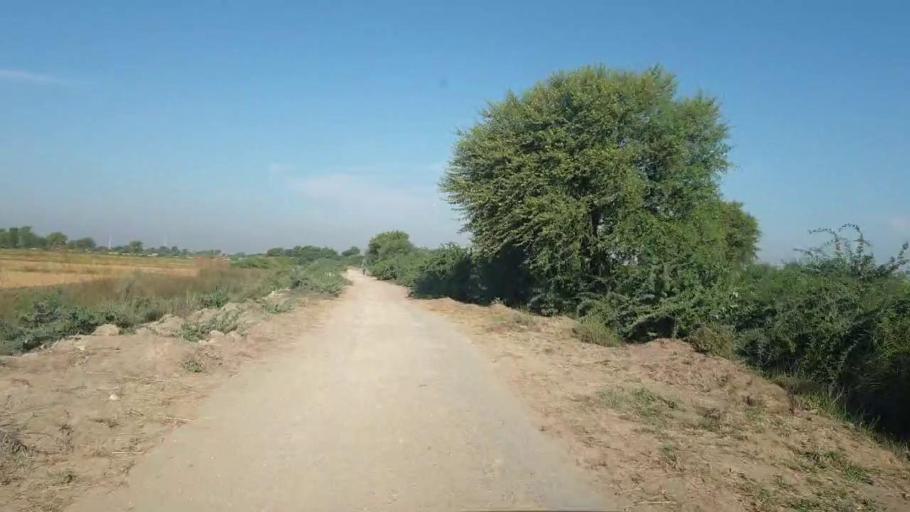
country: PK
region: Sindh
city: Talhar
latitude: 24.8256
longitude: 68.8213
